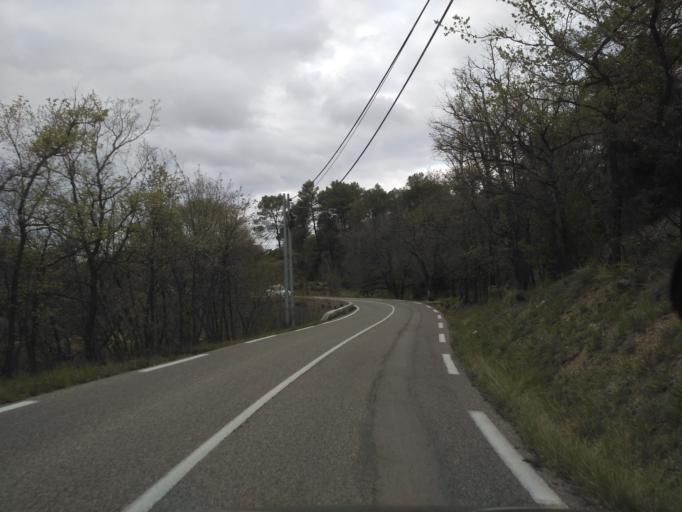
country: FR
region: Provence-Alpes-Cote d'Azur
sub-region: Departement du Var
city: Barjols
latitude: 43.6078
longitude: 5.9513
